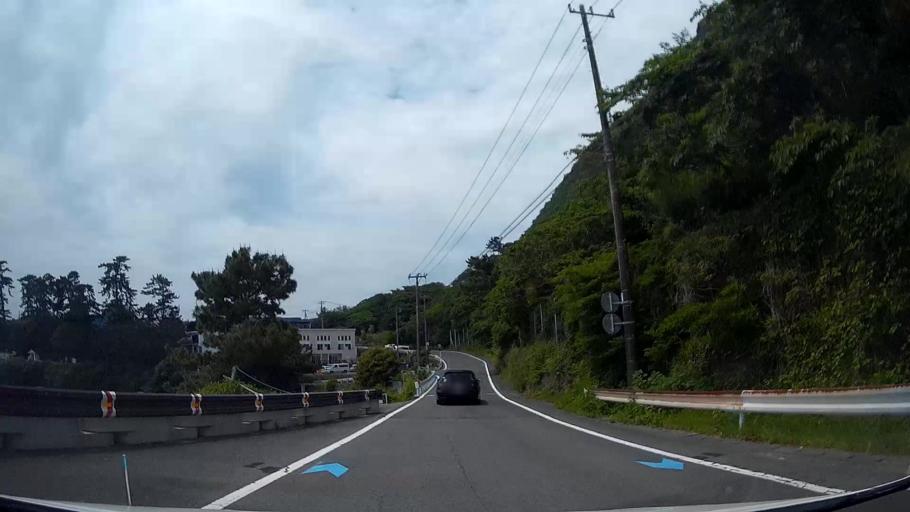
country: JP
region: Shizuoka
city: Ito
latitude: 34.8994
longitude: 139.1318
